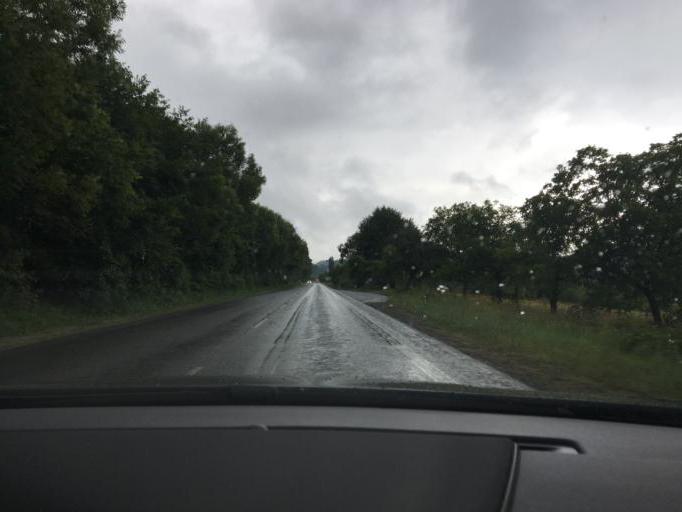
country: BG
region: Kyustendil
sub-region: Obshtina Kyustendil
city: Kyustendil
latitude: 42.2648
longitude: 22.5977
